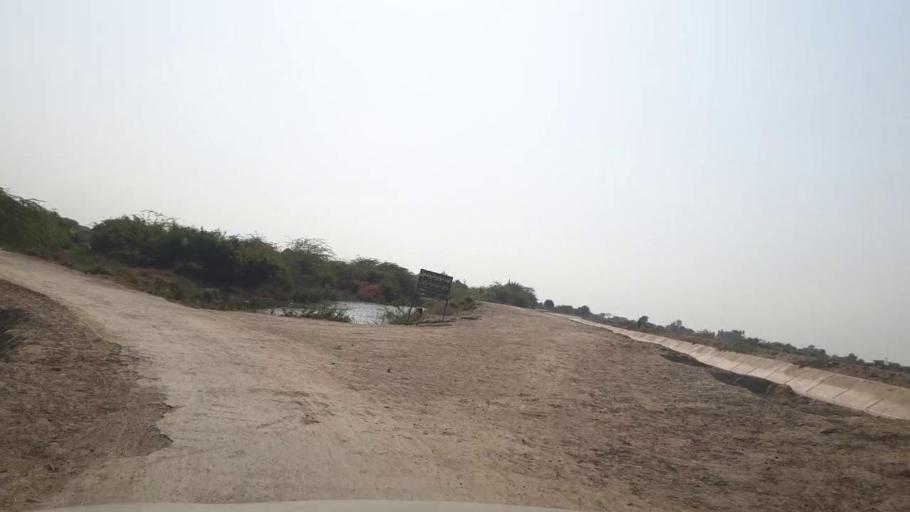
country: PK
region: Sindh
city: Dhoro Naro
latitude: 25.4766
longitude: 69.6468
